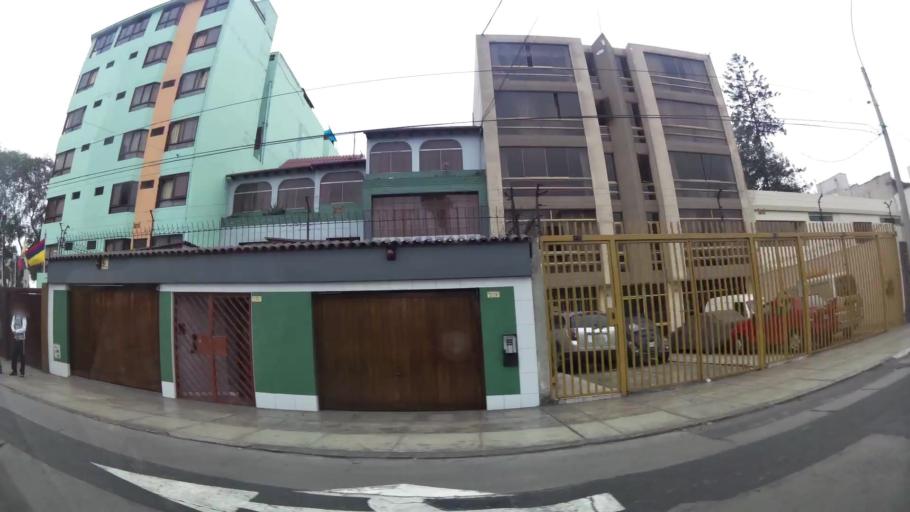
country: PE
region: Lima
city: Lima
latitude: -12.0697
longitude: -77.0615
